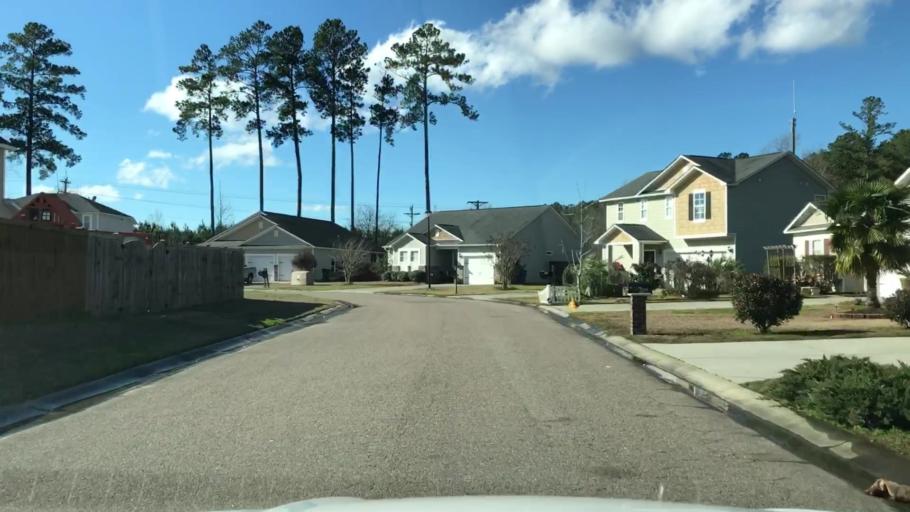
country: US
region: South Carolina
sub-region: Dorchester County
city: Summerville
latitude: 33.0913
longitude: -80.1965
